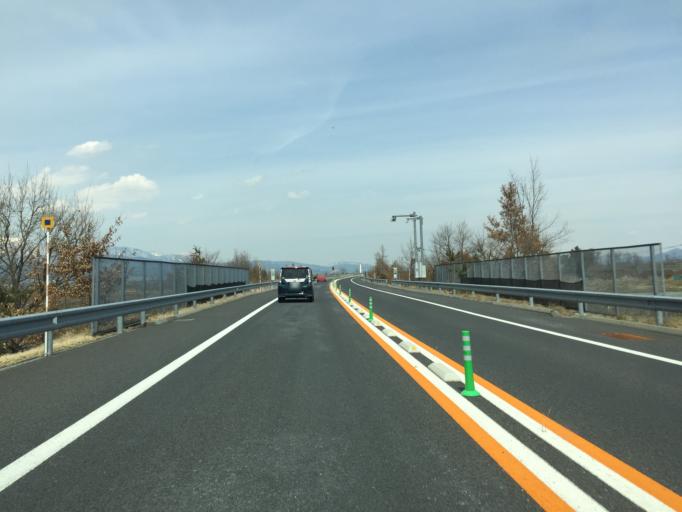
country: JP
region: Yamagata
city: Tendo
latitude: 38.3906
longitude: 140.3429
